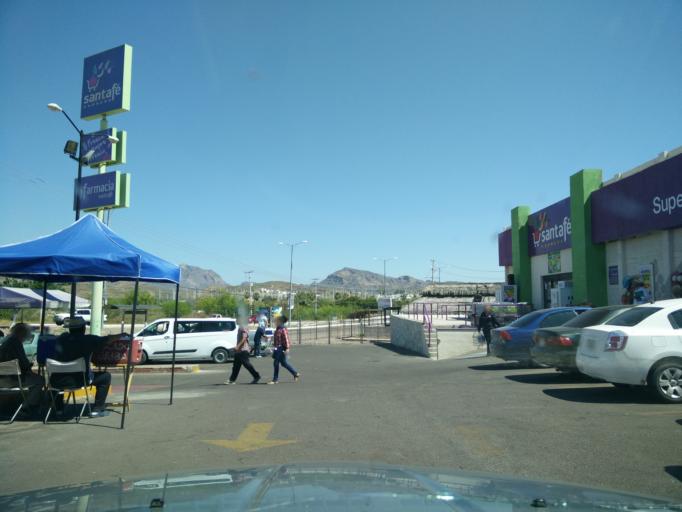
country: MX
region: Sonora
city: Heroica Guaymas
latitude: 27.9512
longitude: -111.0521
